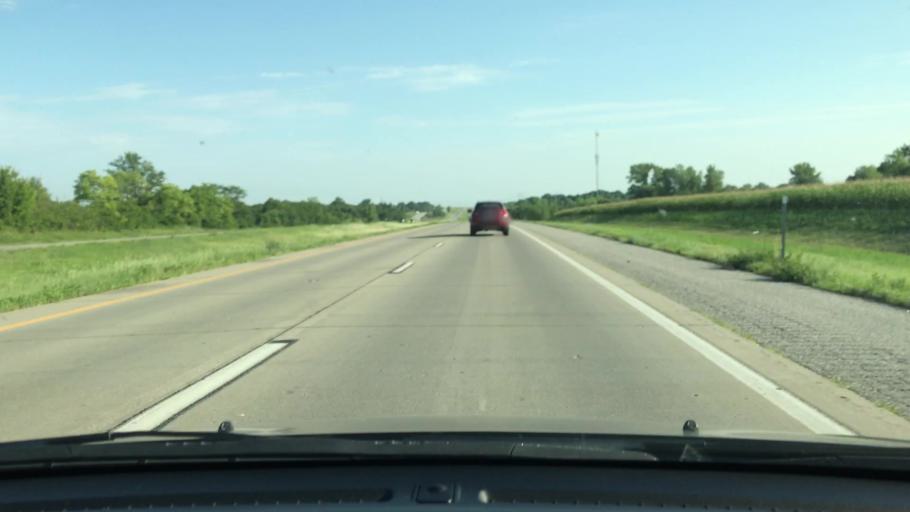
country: US
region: Missouri
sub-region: Jackson County
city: Lees Summit
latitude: 38.8746
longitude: -94.3747
